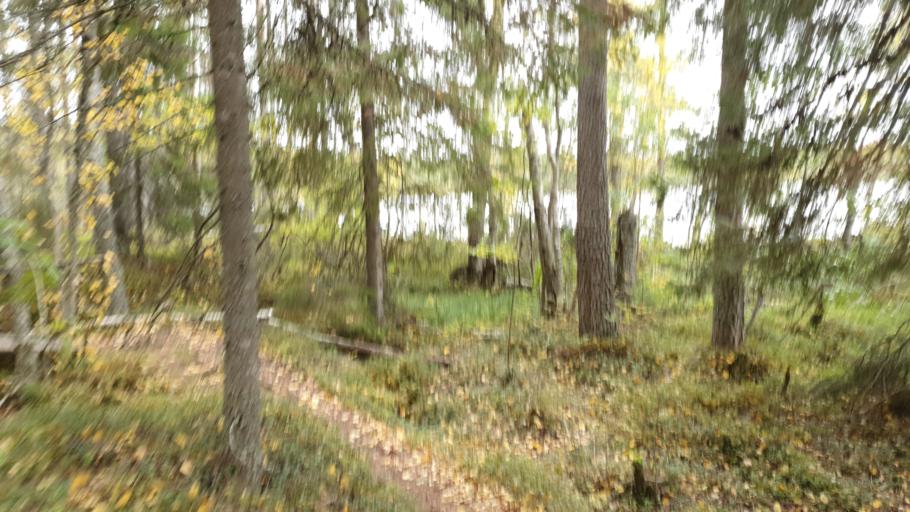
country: FI
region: Kainuu
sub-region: Kehys-Kainuu
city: Kuhmo
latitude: 64.2927
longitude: 29.3237
